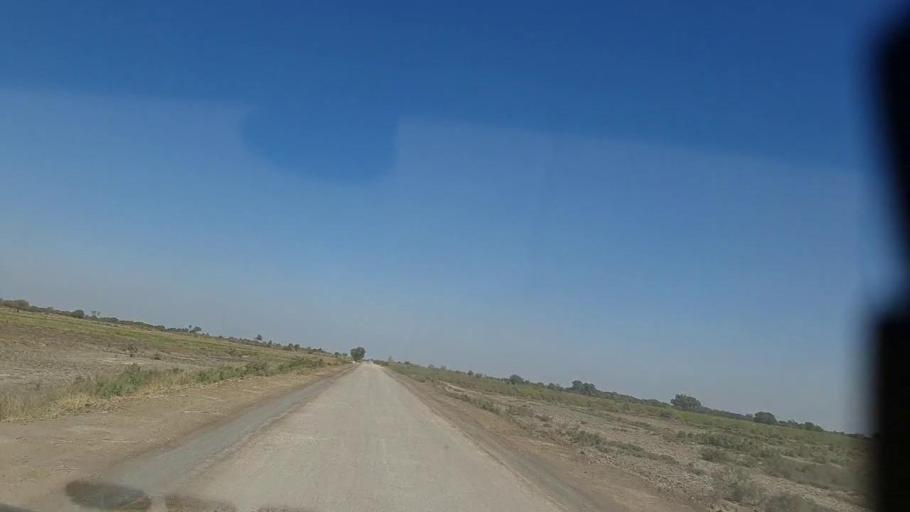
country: PK
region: Sindh
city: Mirwah Gorchani
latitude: 25.2639
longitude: 69.0539
